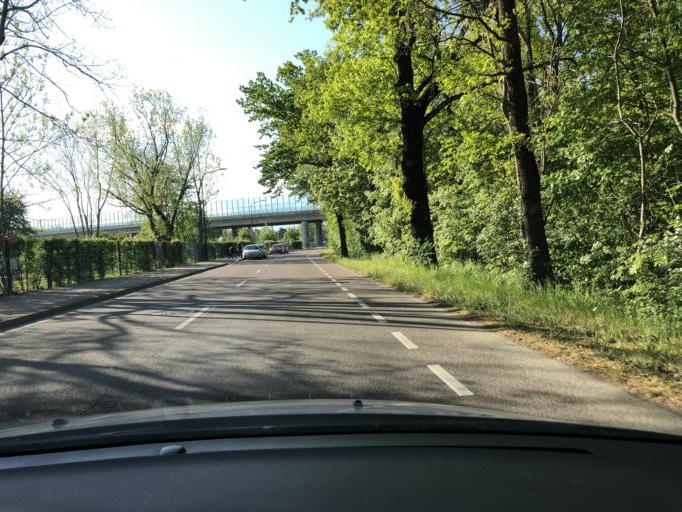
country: DE
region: Saxony
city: Markkleeberg
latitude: 51.2467
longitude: 12.3819
